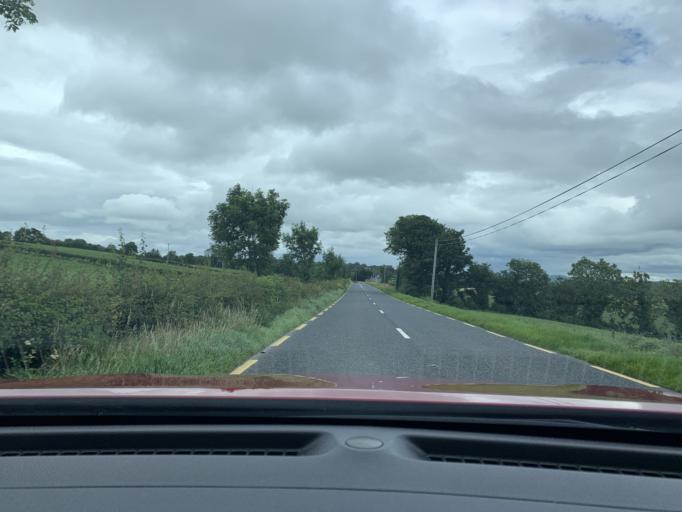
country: IE
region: Ulster
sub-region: County Donegal
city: Convoy
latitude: 54.7986
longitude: -7.6594
